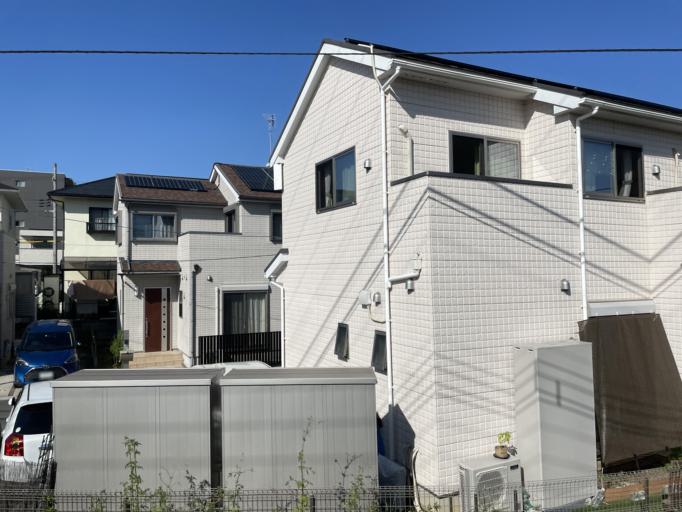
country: JP
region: Nara
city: Nara-shi
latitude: 34.6971
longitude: 135.7767
